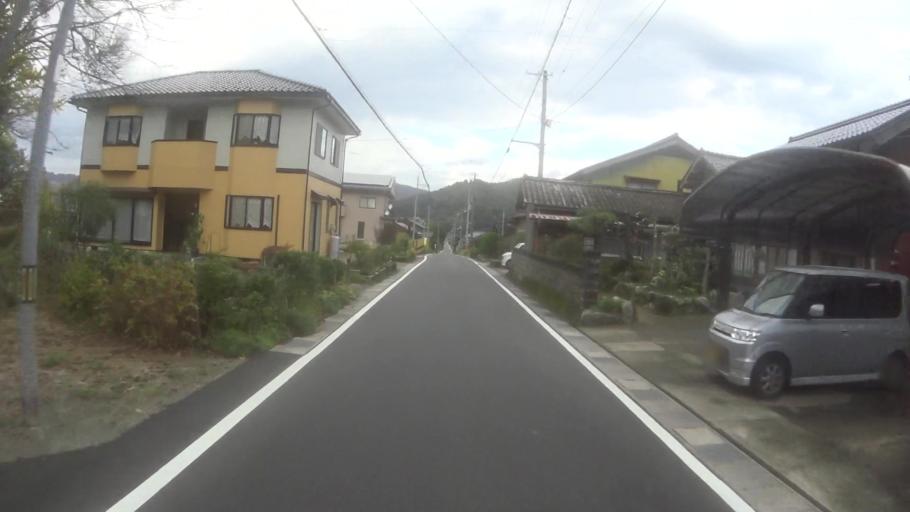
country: JP
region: Kyoto
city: Miyazu
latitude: 35.5221
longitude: 135.1258
